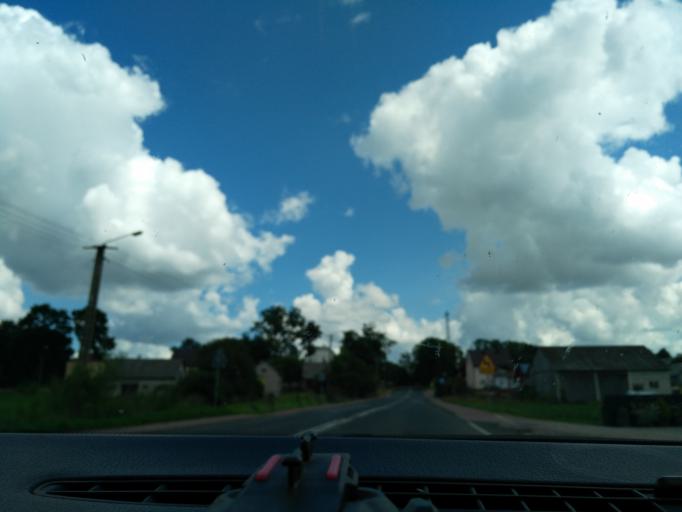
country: PL
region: Podlasie
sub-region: Powiat siemiatycki
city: Dziadkowice
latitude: 52.5635
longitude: 22.9112
